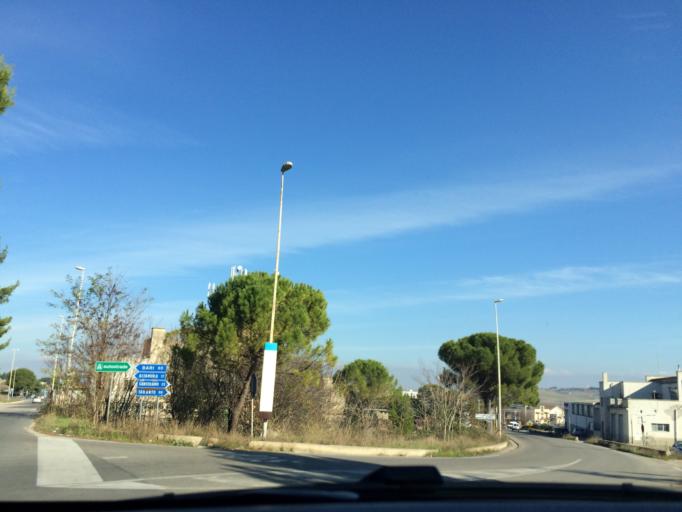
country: IT
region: Basilicate
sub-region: Provincia di Matera
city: Matera
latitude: 40.6817
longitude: 16.5902
